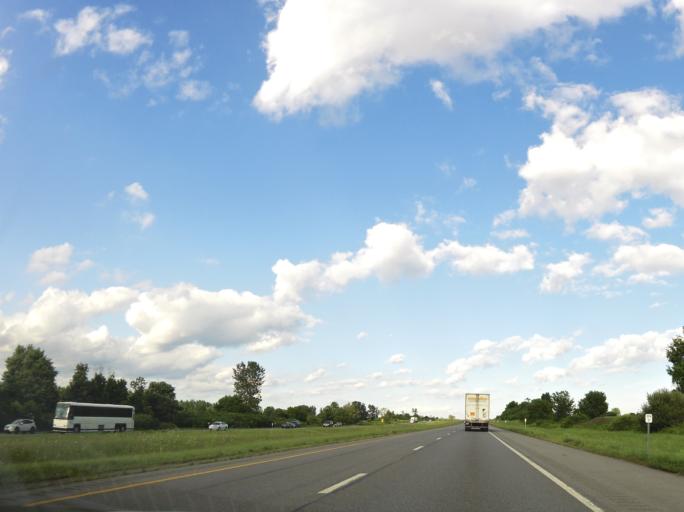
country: US
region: New York
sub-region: Genesee County
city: Oakfield
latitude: 43.0159
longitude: -78.2804
